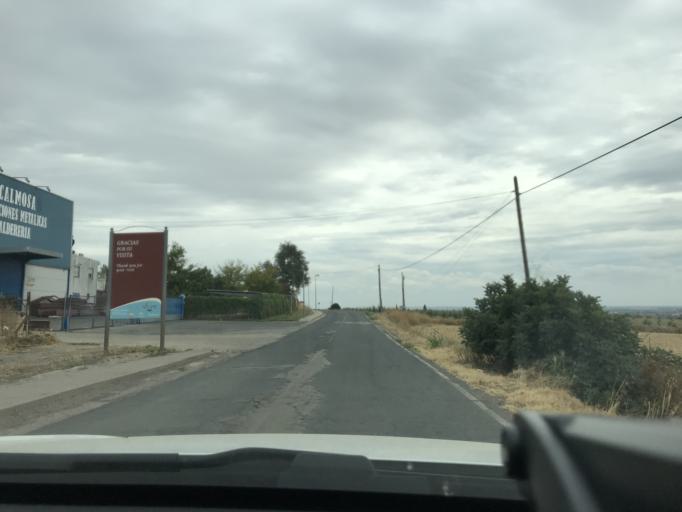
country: ES
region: Andalusia
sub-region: Provincia de Sevilla
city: Villanueva del Rio y Minas
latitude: 37.6455
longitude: -5.7084
